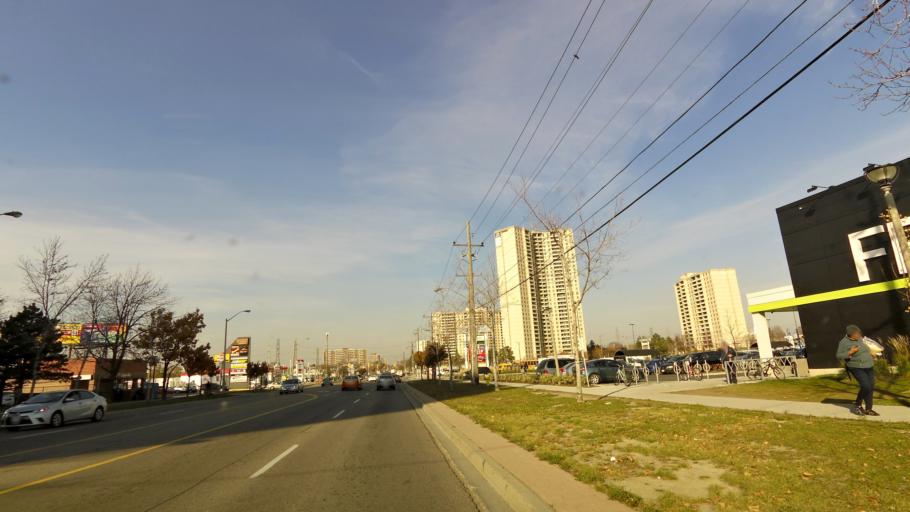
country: CA
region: Ontario
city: Concord
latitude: 43.7556
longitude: -79.5171
